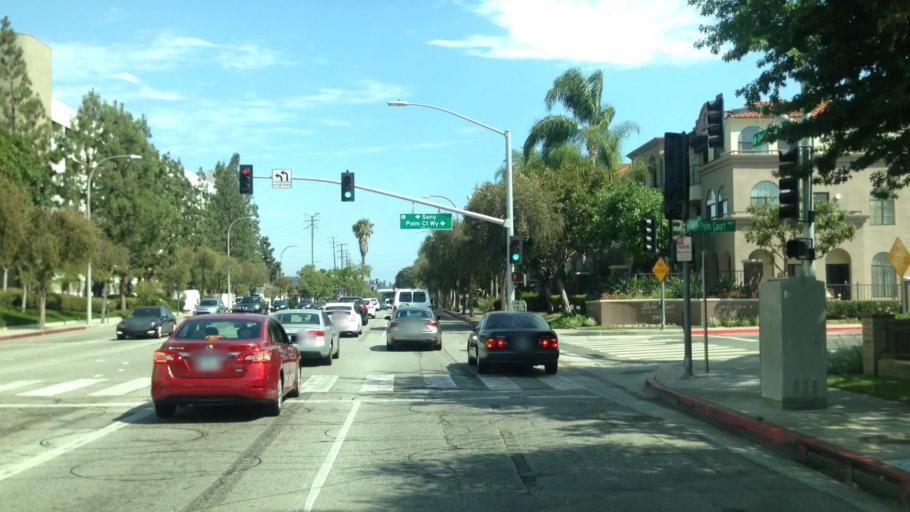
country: US
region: California
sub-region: Los Angeles County
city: Culver City
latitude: 34.0159
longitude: -118.4045
